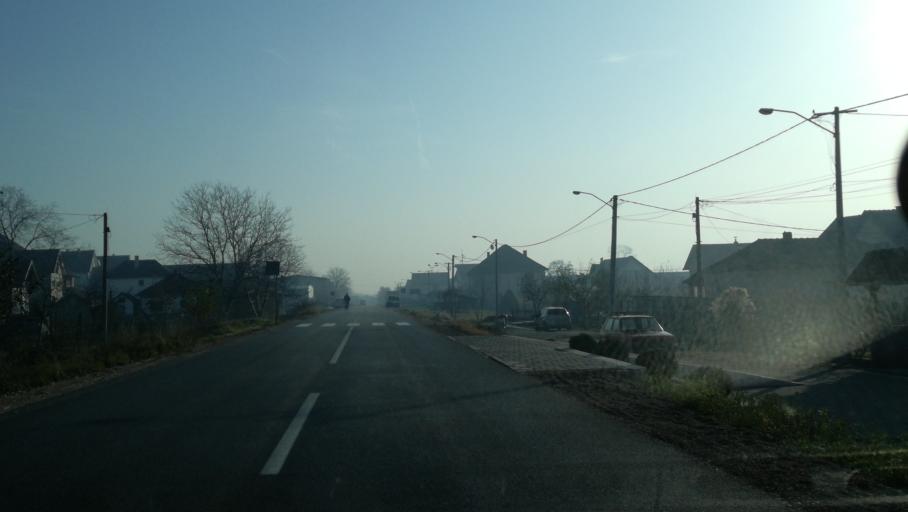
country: RS
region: Central Serbia
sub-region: Moravicki Okrug
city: Cacak
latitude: 43.9002
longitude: 20.3853
